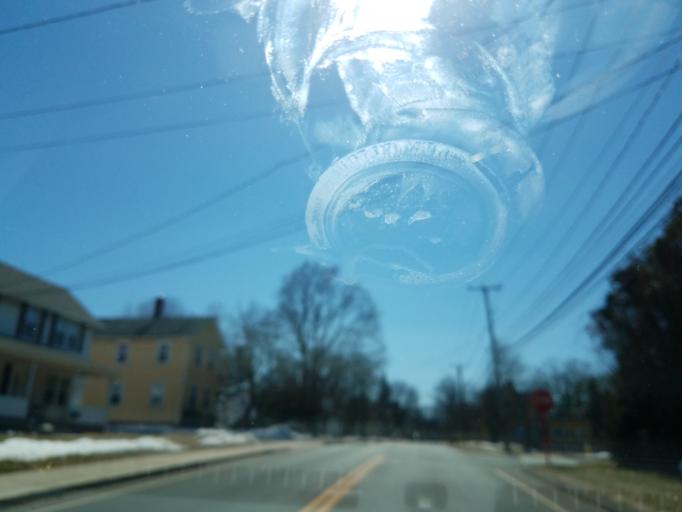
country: US
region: Connecticut
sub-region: Hartford County
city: Windsor Locks
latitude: 41.9232
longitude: -72.6333
